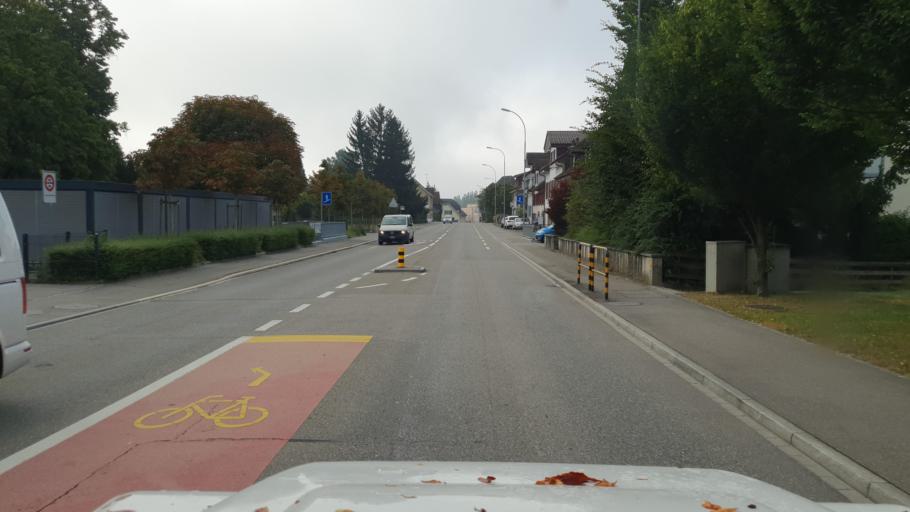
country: CH
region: Aargau
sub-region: Bezirk Baden
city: Mellingen
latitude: 47.4222
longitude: 8.2730
